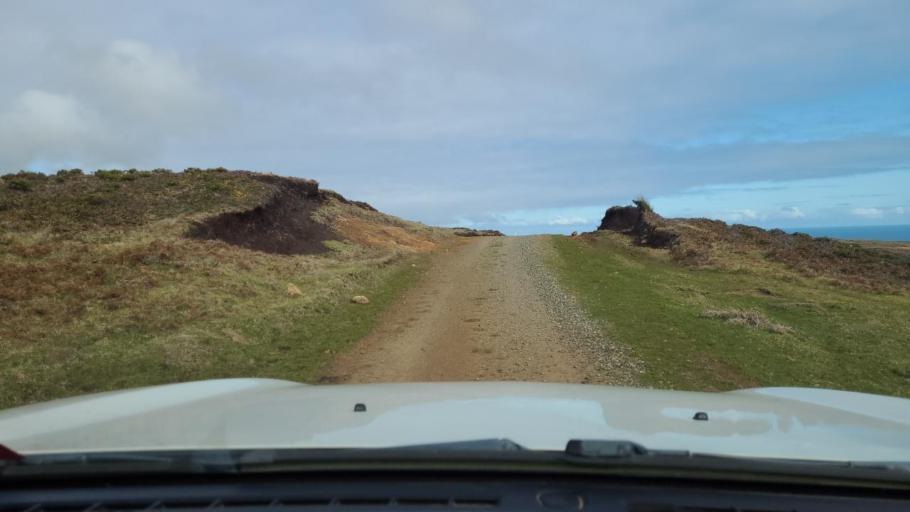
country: NZ
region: Chatham Islands
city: Waitangi
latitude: -44.0534
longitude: -176.6333
